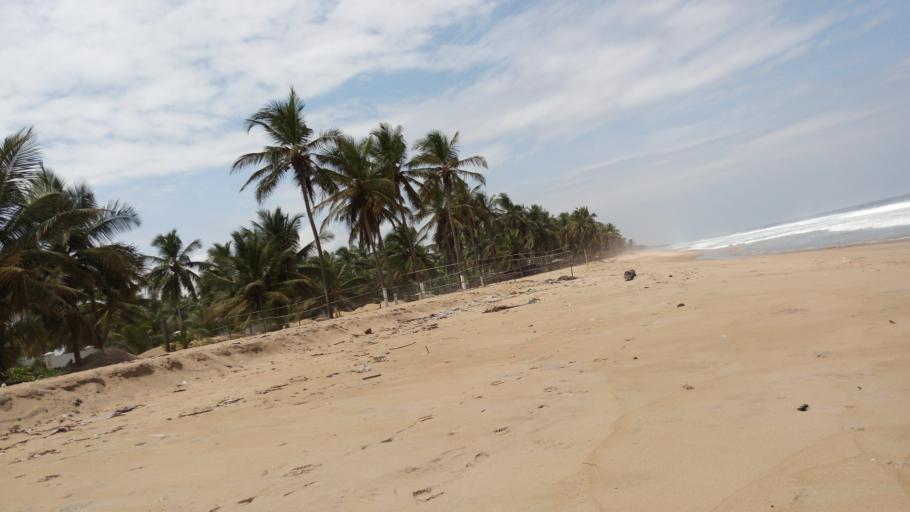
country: CI
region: Sud-Comoe
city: Grand-Bassam
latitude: 5.1876
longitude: -3.6960
